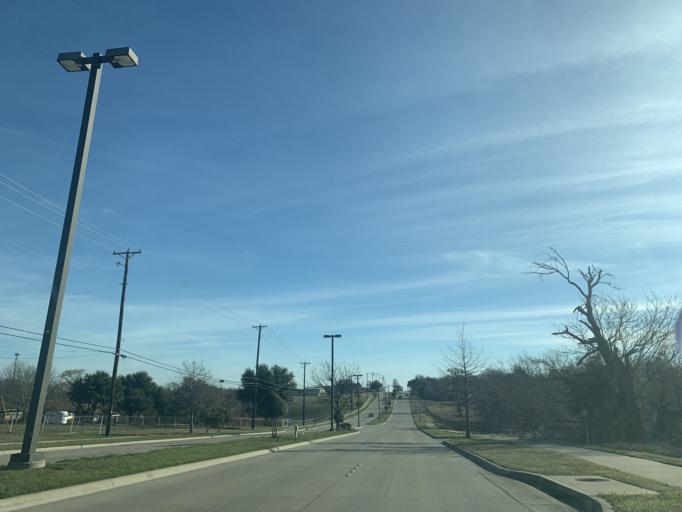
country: US
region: Texas
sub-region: Dallas County
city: DeSoto
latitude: 32.5751
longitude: -96.8321
